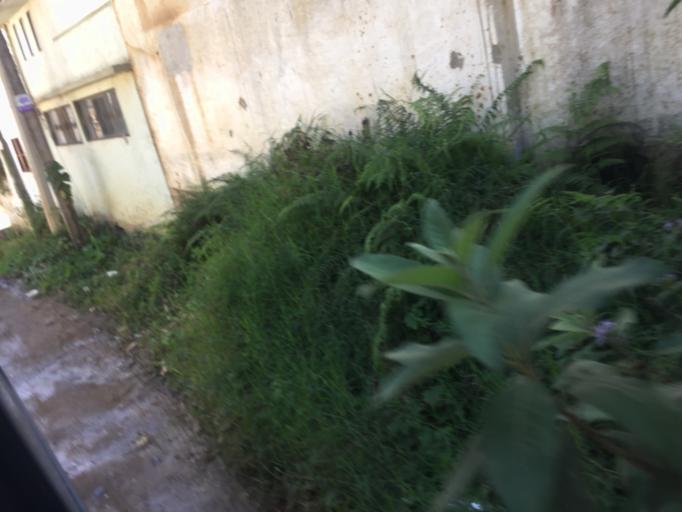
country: MX
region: Veracruz
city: El Castillo
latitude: 19.5317
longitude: -96.8841
